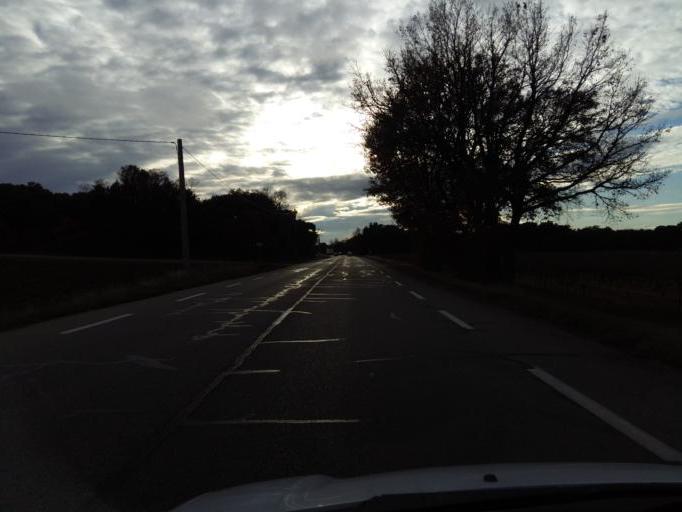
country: FR
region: Provence-Alpes-Cote d'Azur
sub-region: Departement du Vaucluse
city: Visan
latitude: 44.3440
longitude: 4.9523
